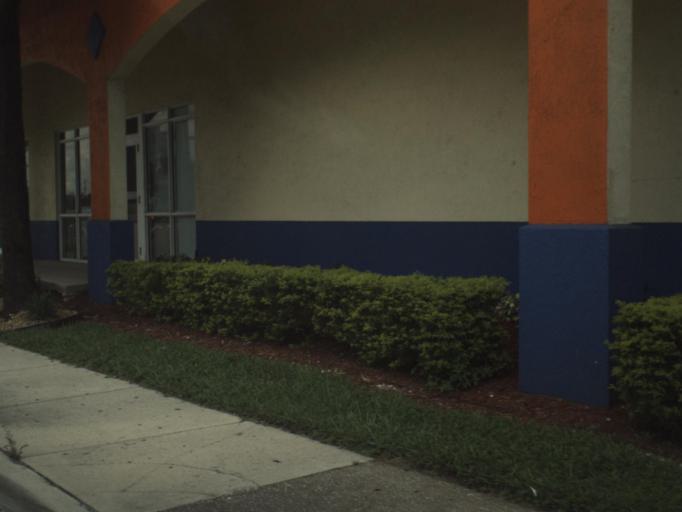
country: US
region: Florida
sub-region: Miami-Dade County
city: North Miami Beach
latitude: 25.9283
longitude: -80.1817
